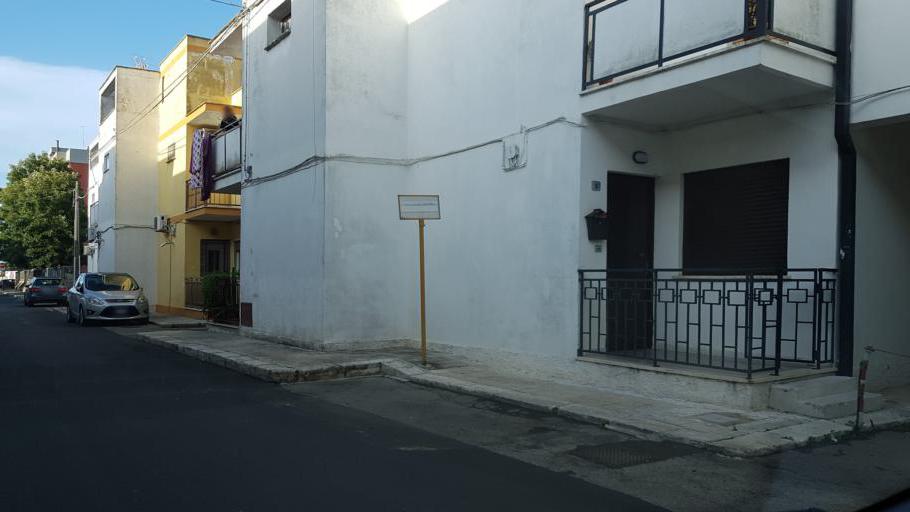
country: IT
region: Apulia
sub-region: Provincia di Brindisi
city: Oria
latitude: 40.5055
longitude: 17.6510
